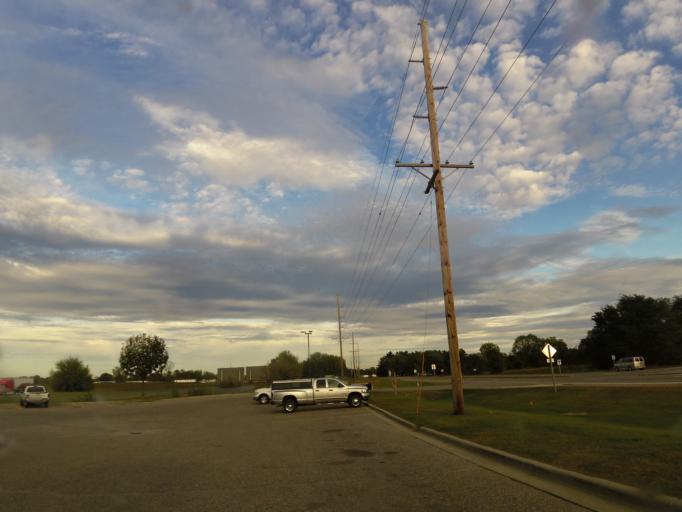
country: US
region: Wisconsin
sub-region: Juneau County
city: Mauston
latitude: 43.7967
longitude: -90.0509
